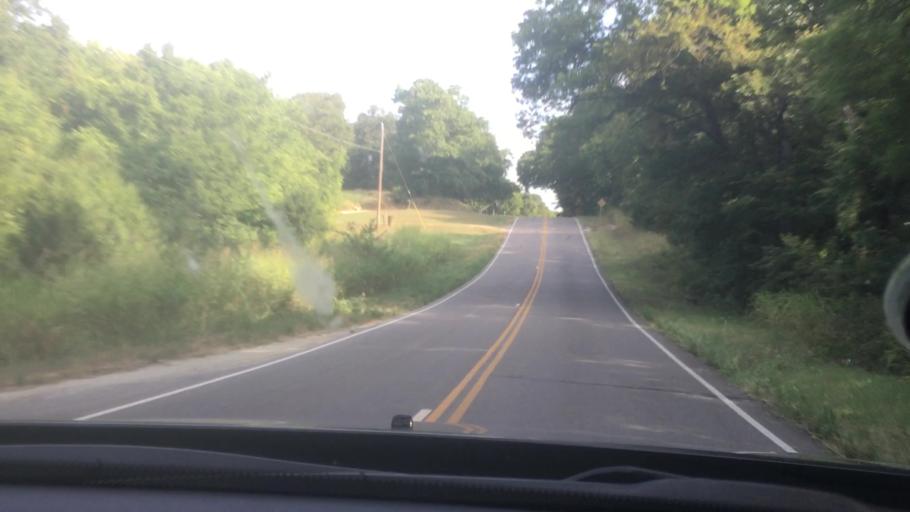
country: US
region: Oklahoma
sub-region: Pontotoc County
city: Ada
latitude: 34.7340
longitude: -96.6704
